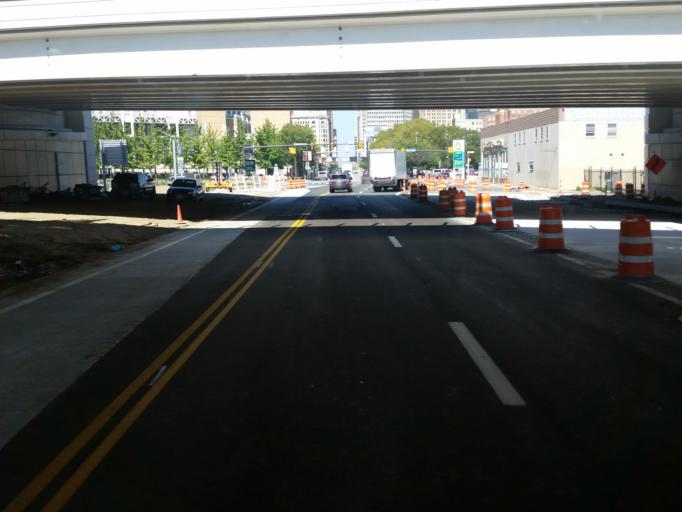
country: US
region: Ohio
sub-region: Cuyahoga County
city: Cleveland
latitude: 41.4947
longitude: -81.6817
